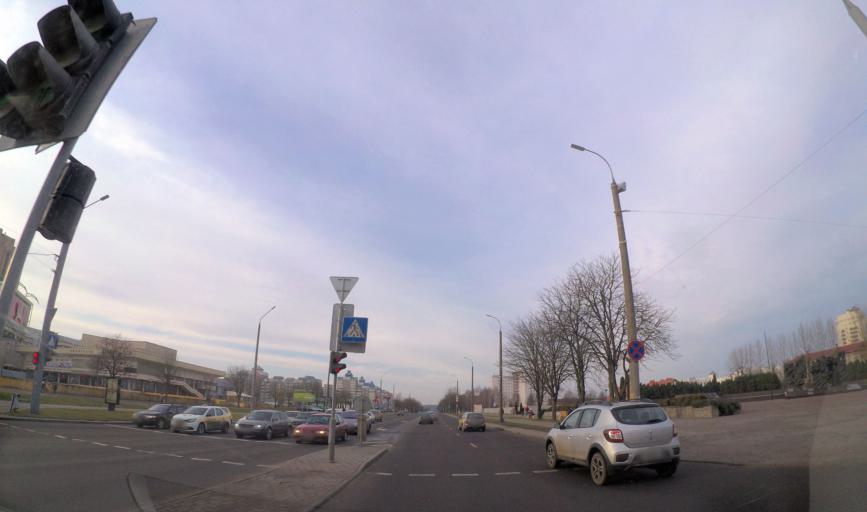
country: BY
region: Grodnenskaya
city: Hrodna
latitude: 53.6720
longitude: 23.8030
